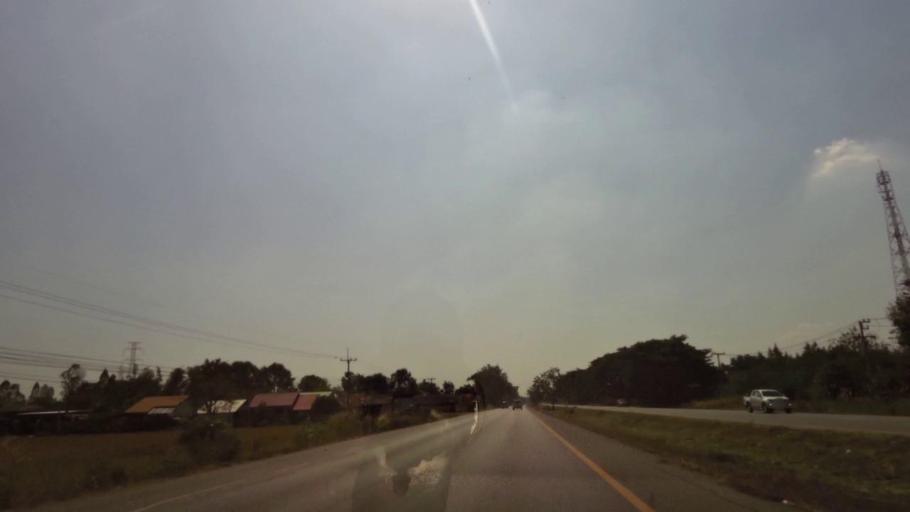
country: TH
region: Phichit
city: Wachira Barami
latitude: 16.3883
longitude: 100.1381
